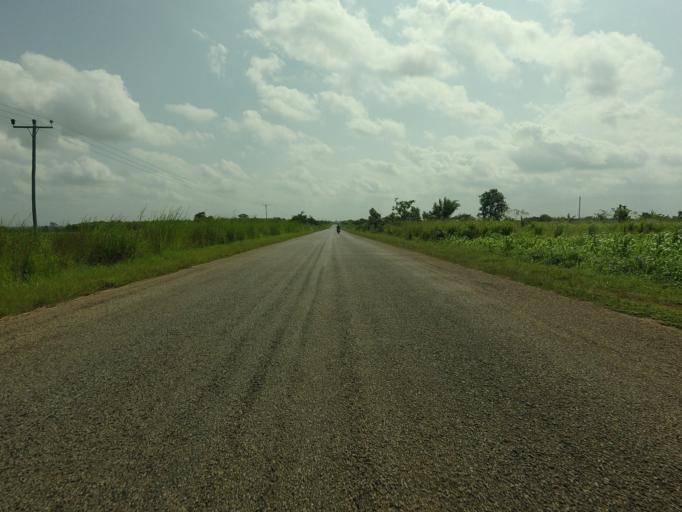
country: TG
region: Maritime
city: Tsevie
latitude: 6.3921
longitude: 0.8297
